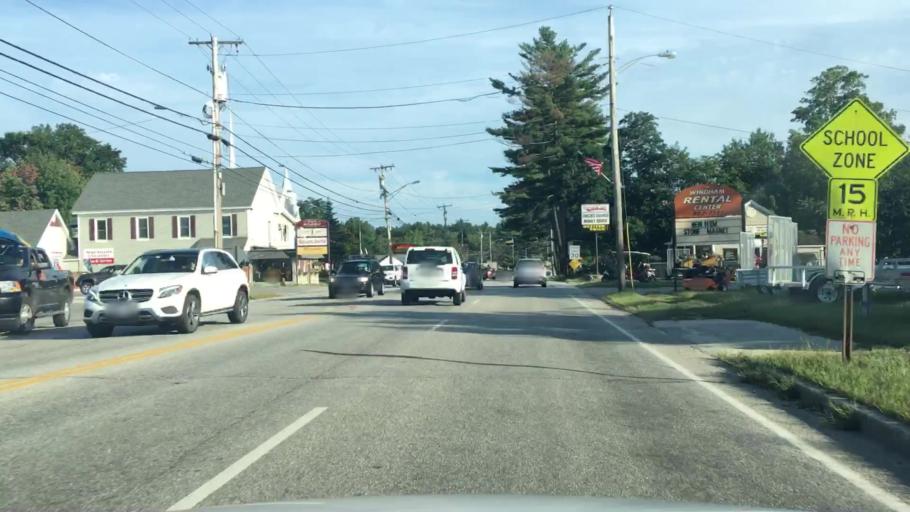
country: US
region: Maine
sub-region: Cumberland County
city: North Windham
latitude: 43.8330
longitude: -70.4373
